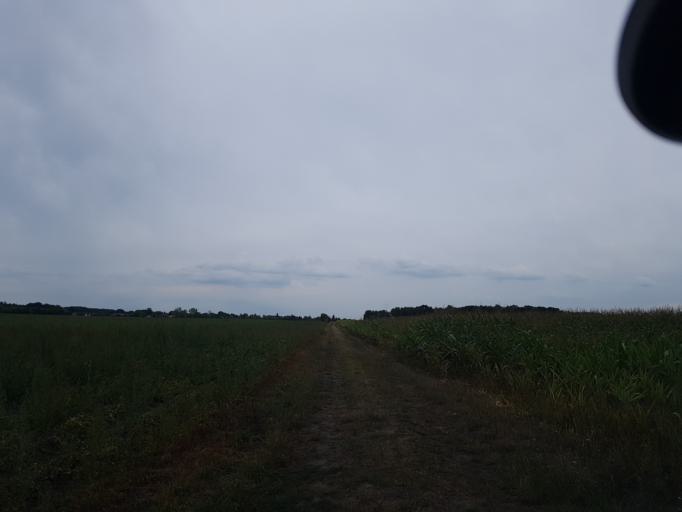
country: DE
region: Brandenburg
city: Ruckersdorf
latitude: 51.6037
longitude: 13.6318
